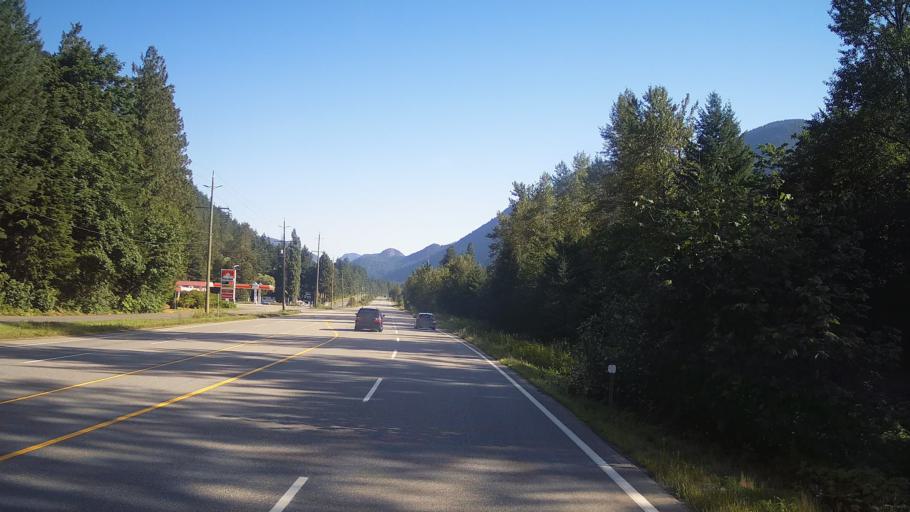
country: CA
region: British Columbia
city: Hope
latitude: 49.4863
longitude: -121.4213
